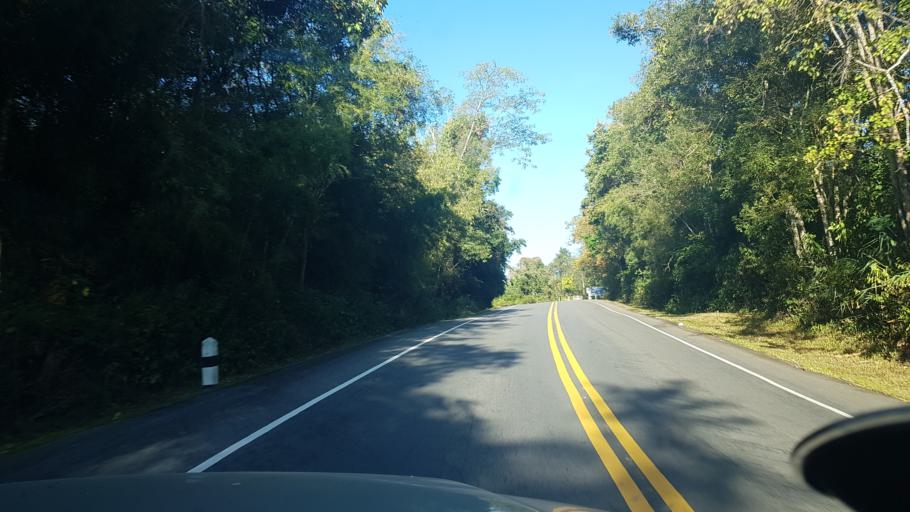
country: TH
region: Phetchabun
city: Nam Nao
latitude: 16.7609
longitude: 101.4754
